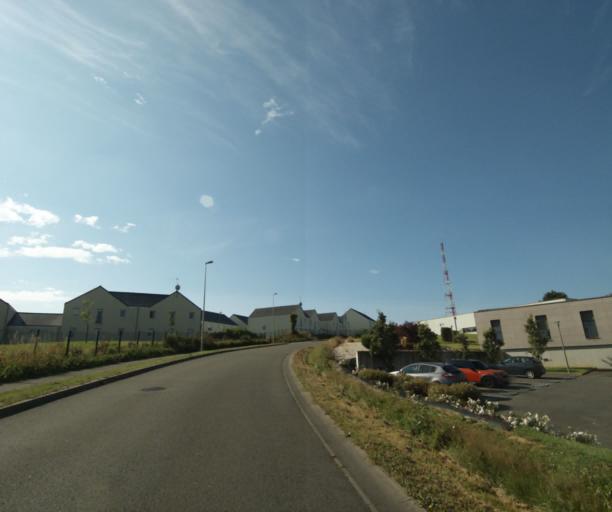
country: FR
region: Pays de la Loire
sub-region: Departement de la Mayenne
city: Laval
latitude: 48.0578
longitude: -0.7854
